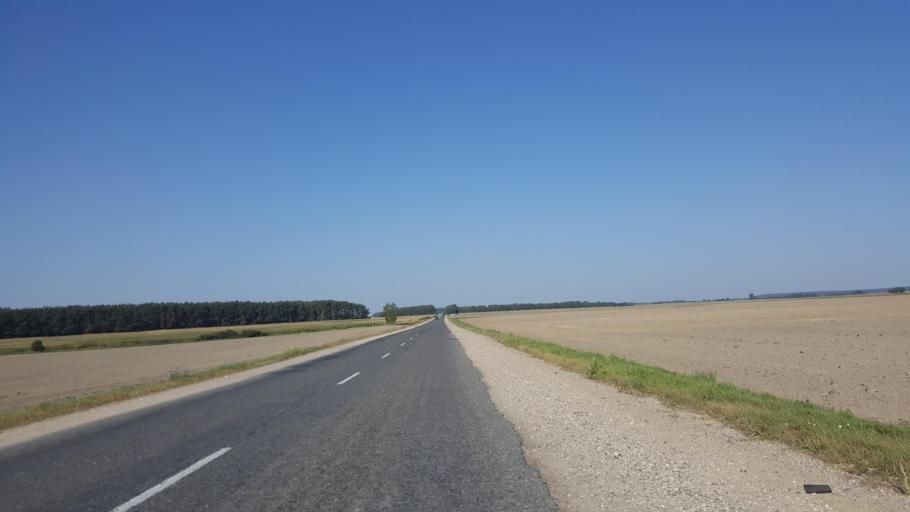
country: BY
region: Brest
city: Kamyanyets
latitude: 52.4051
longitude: 23.7542
